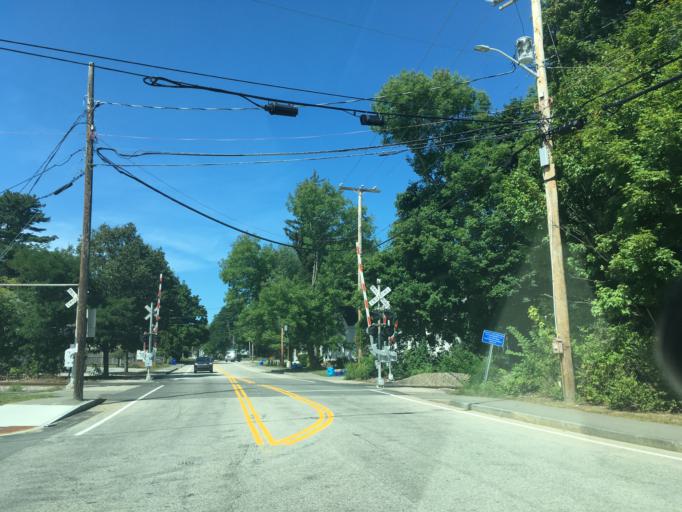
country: US
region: New Hampshire
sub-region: Rockingham County
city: Exeter
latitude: 42.9827
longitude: -70.9570
